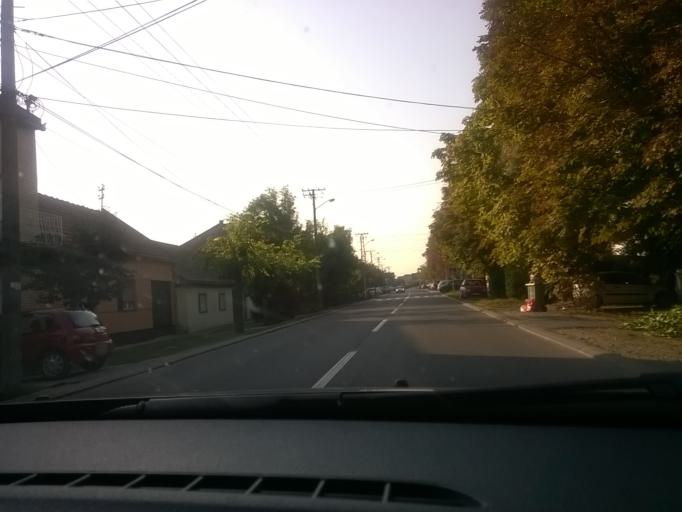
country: RS
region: Autonomna Pokrajina Vojvodina
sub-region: Juznobanatski Okrug
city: Vrsac
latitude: 45.1187
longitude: 21.2845
